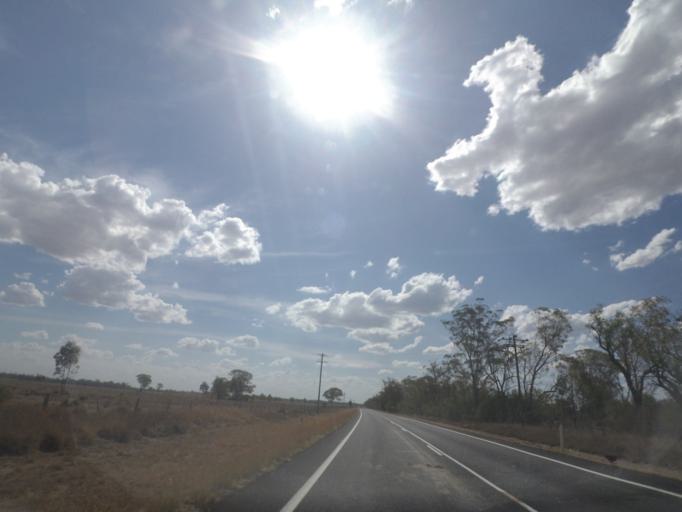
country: AU
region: New South Wales
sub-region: Moree Plains
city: Boggabilla
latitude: -28.4129
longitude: 151.1129
